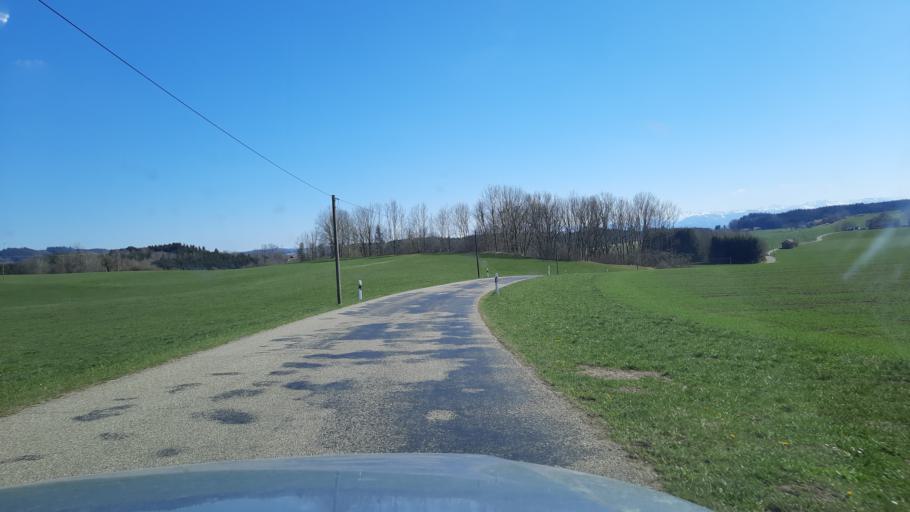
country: DE
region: Bavaria
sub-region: Swabia
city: Wolfertschwenden
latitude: 47.8571
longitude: 10.2469
